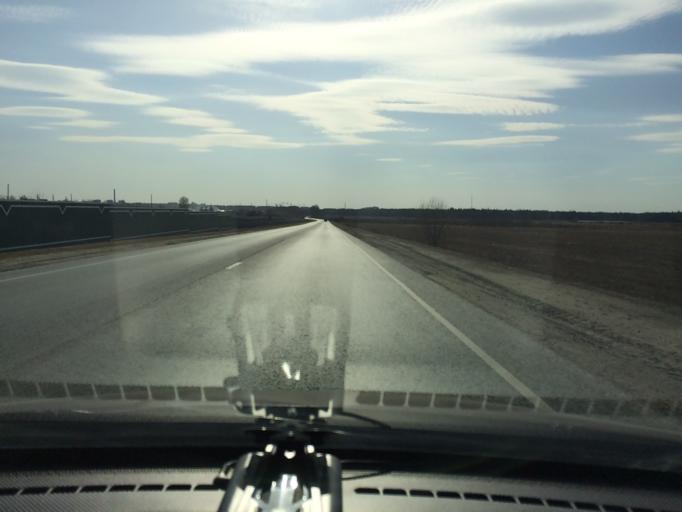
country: RU
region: Mariy-El
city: Yoshkar-Ola
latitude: 56.6577
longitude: 47.9663
